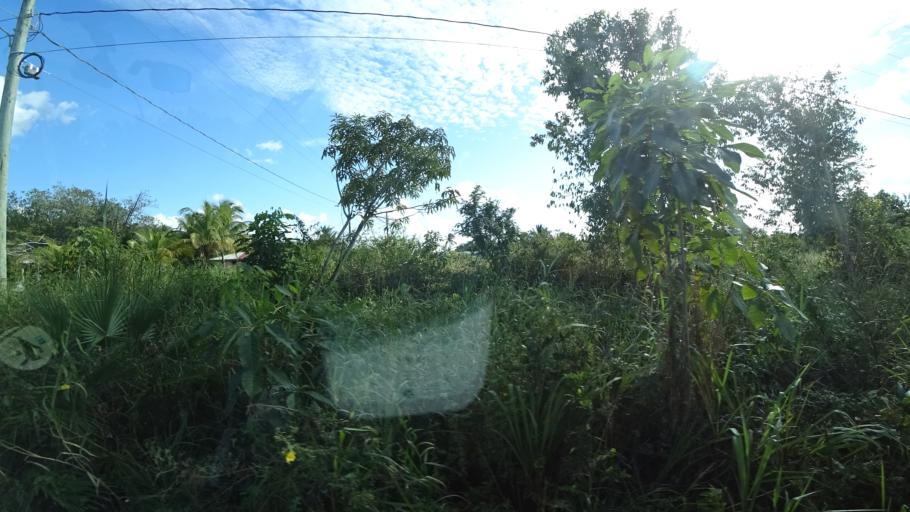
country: BZ
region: Belize
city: Belize City
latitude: 17.5559
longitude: -88.3997
